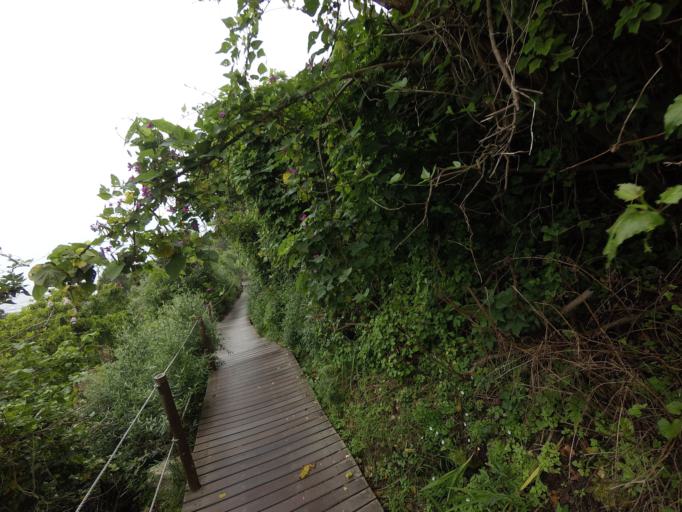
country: ZA
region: Eastern Cape
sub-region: Cacadu District Municipality
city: Kareedouw
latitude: -34.0200
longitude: 23.9013
